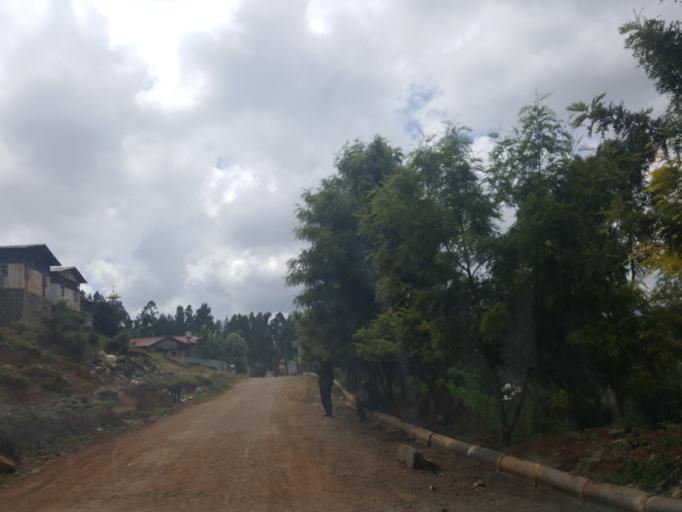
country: ET
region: Adis Abeba
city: Addis Ababa
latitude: 9.0701
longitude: 38.7386
